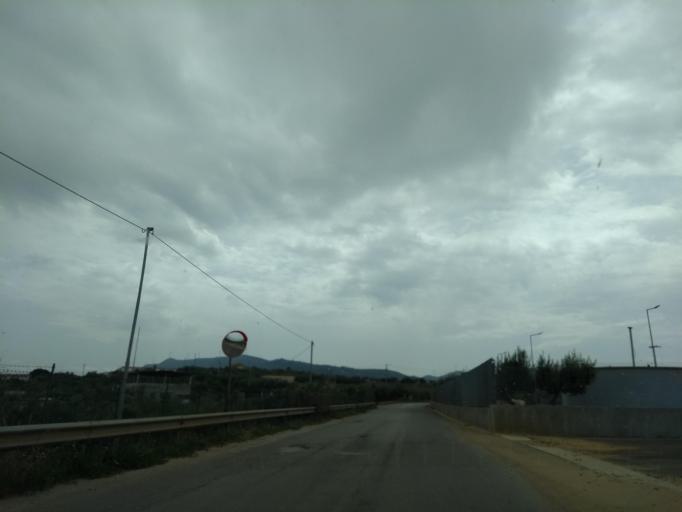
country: IT
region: Sicily
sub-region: Palermo
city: Partinico
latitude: 38.0028
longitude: 13.0682
